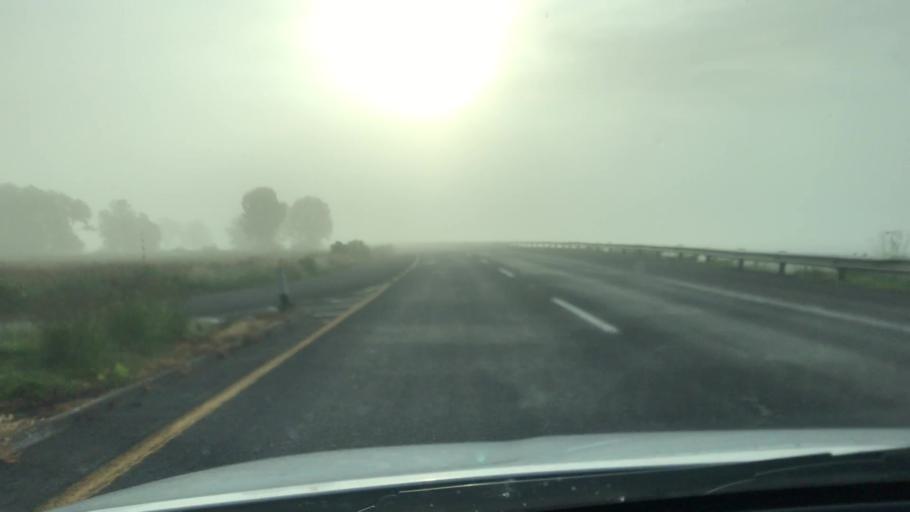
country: MX
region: Jalisco
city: Tepatitlan de Morelos
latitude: 20.8989
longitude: -102.7001
